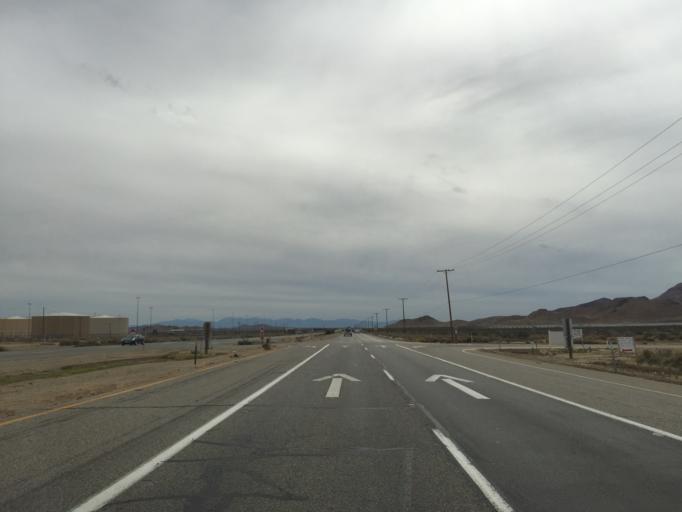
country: US
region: California
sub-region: Kern County
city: Mojave
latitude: 35.0326
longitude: -118.1685
